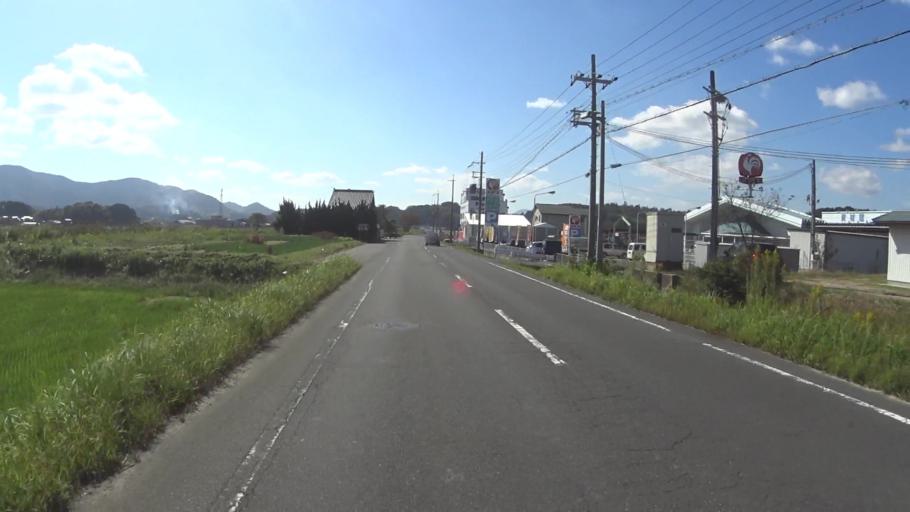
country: JP
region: Kyoto
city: Miyazu
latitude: 35.6694
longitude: 135.0867
